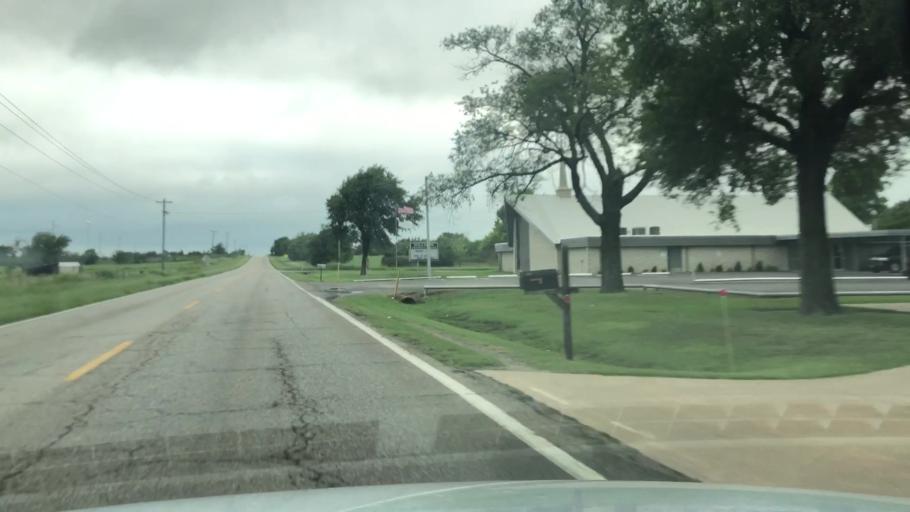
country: US
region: Oklahoma
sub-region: Nowata County
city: Nowata
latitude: 36.7065
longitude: -95.6535
